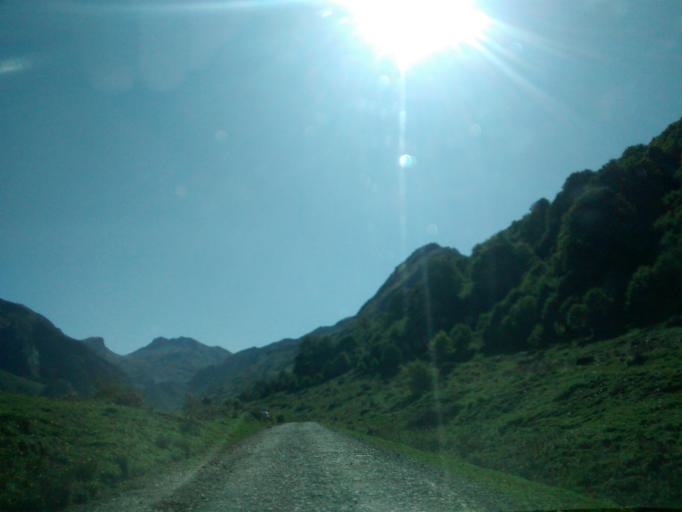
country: ES
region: Aragon
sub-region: Provincia de Huesca
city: Aragues del Puerto
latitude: 42.8485
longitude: -0.6704
